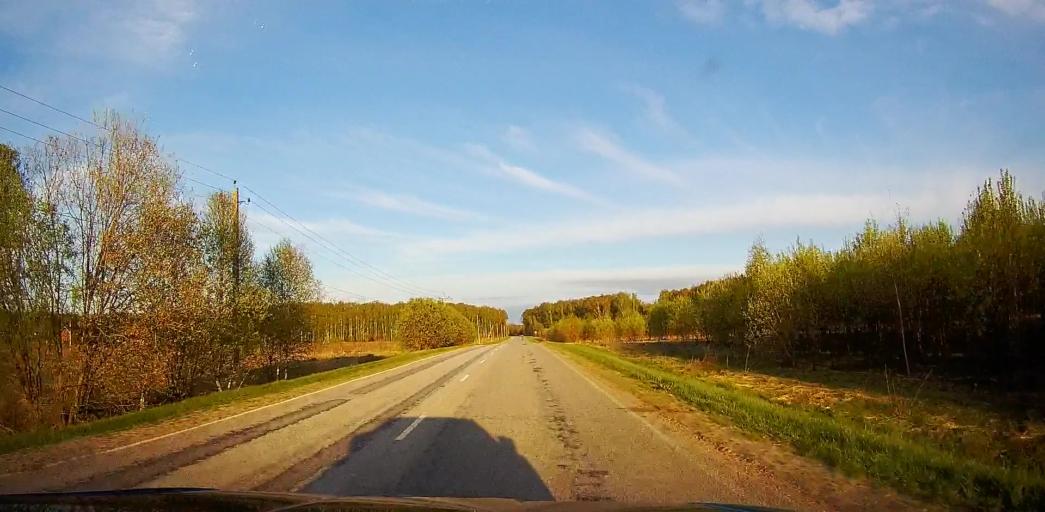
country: RU
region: Moskovskaya
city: Meshcherino
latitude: 55.2298
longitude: 38.3787
